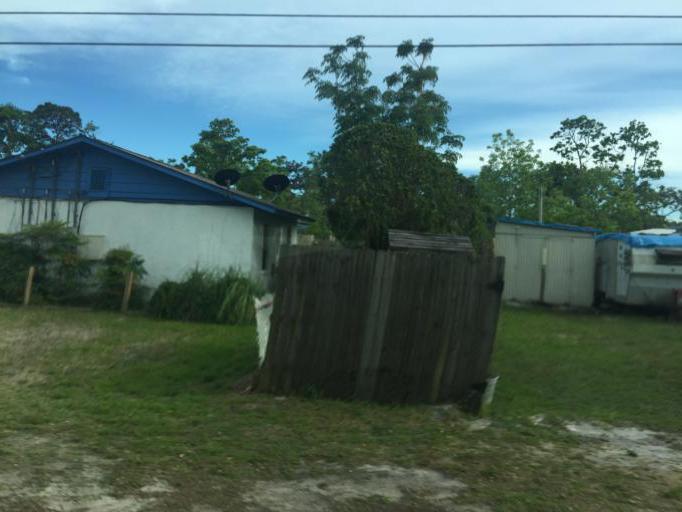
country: US
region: Florida
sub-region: Bay County
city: Panama City Beach
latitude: 30.1784
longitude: -85.7808
